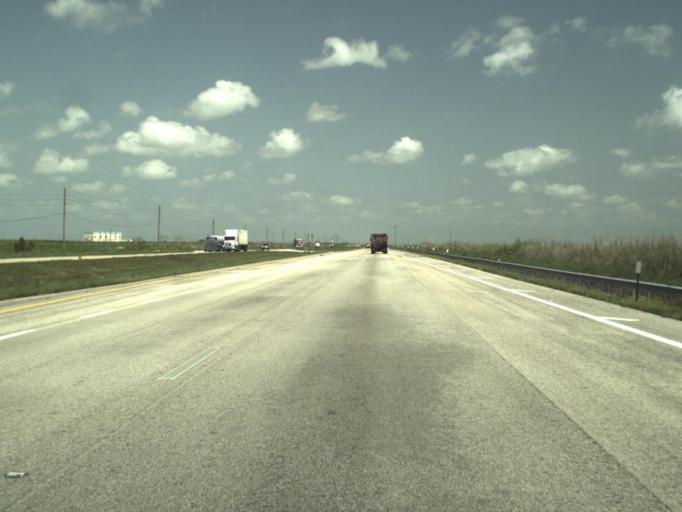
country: US
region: Florida
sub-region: Palm Beach County
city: Belle Glade Camp
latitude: 26.3871
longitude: -80.5780
